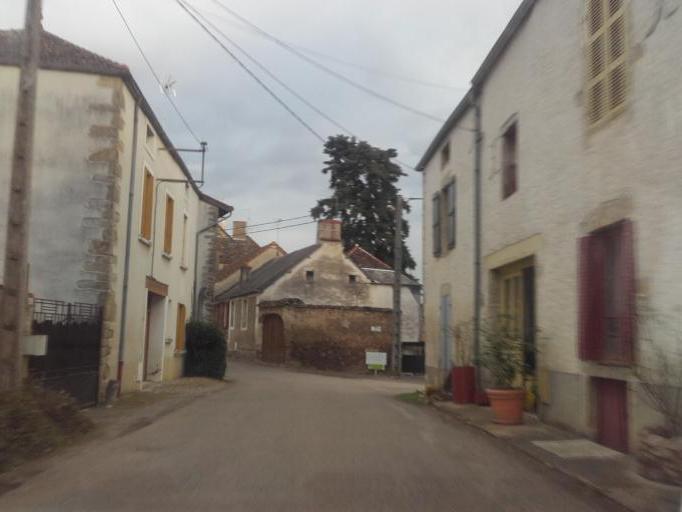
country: FR
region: Bourgogne
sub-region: Departement de la Cote-d'Or
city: Nolay
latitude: 46.9062
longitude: 4.6521
